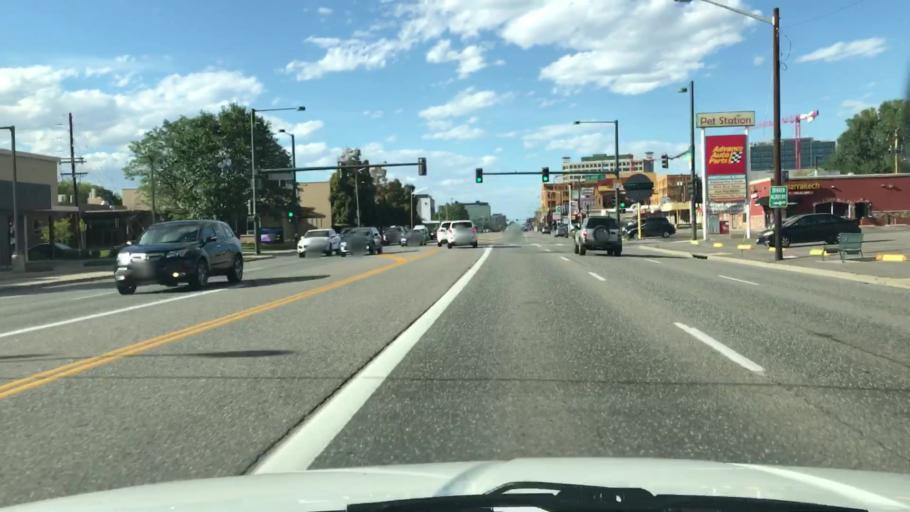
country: US
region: Colorado
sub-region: Arapahoe County
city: Glendale
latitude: 39.6742
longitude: -104.9407
